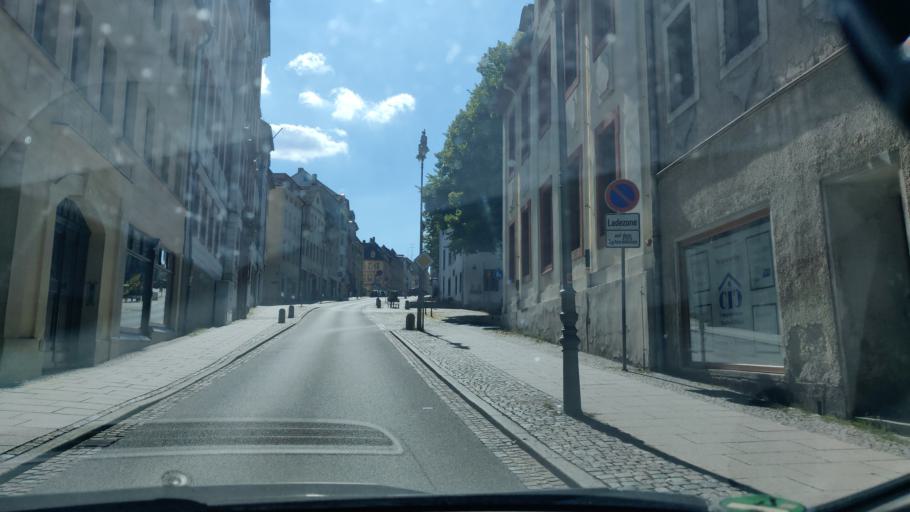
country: DE
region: Thuringia
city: Altenburg
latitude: 50.9868
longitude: 12.4370
